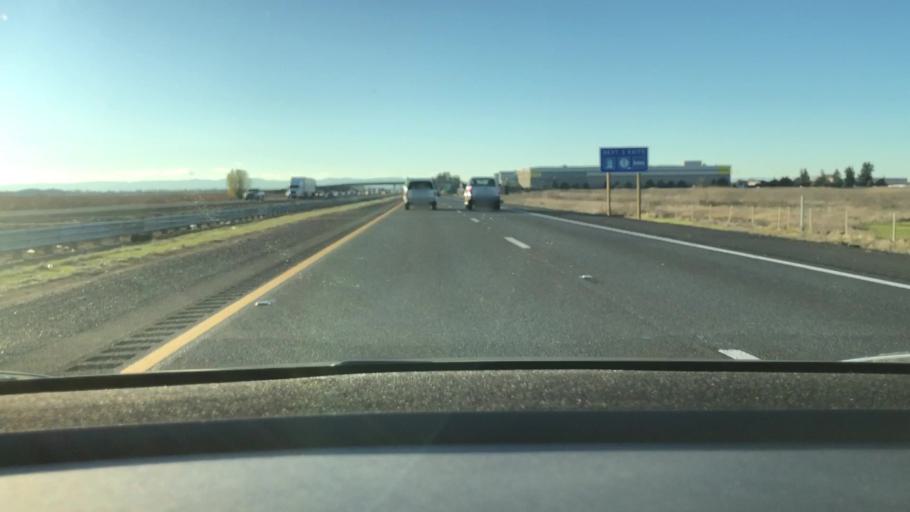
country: US
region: California
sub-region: Yolo County
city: Woodland
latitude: 38.6743
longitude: -121.7036
